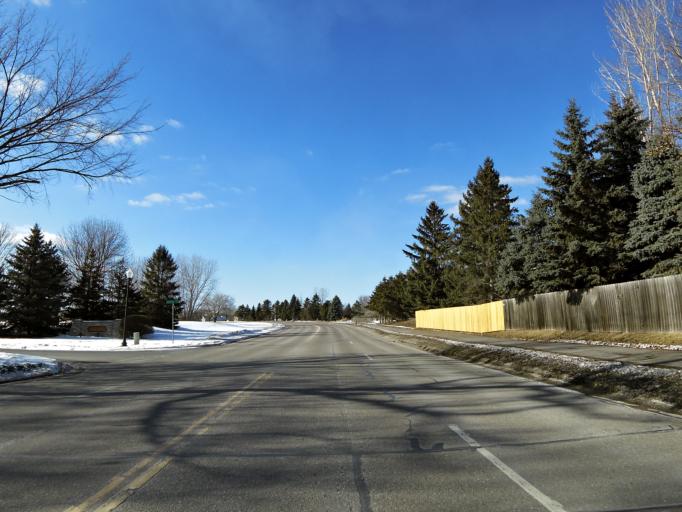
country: US
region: Minnesota
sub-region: Washington County
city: Woodbury
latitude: 44.9041
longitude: -92.9184
